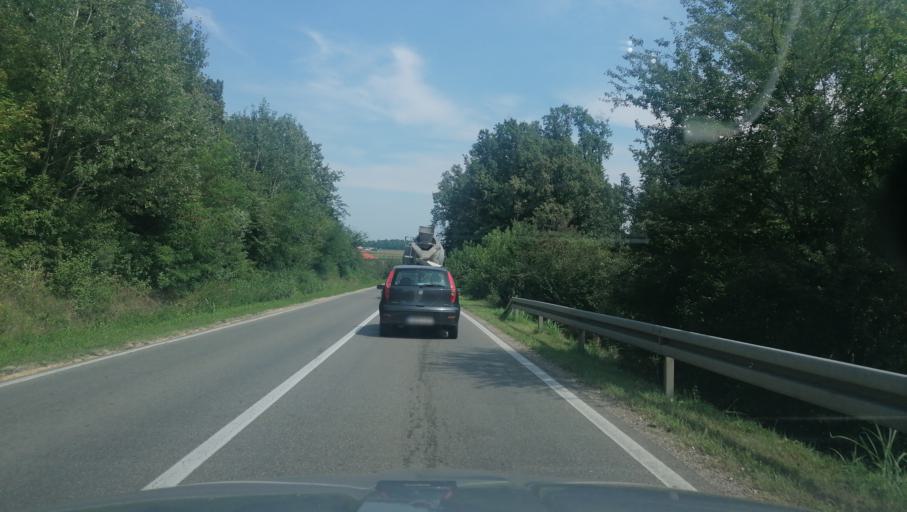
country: BA
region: Republika Srpska
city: Velika Obarska
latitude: 44.7693
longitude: 19.1549
